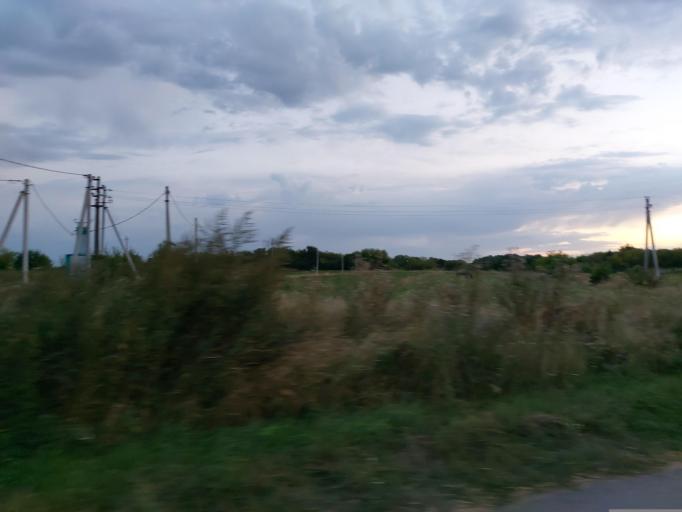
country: RU
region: Lipetsk
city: Dolgorukovo
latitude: 52.3780
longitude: 38.0490
